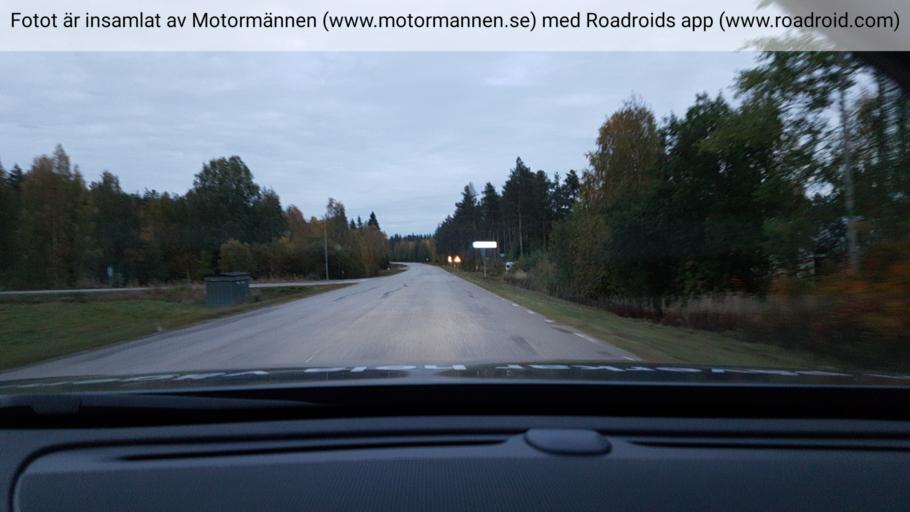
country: SE
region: Norrbotten
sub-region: Alvsbyns Kommun
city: AElvsbyn
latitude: 65.8375
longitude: 20.5152
